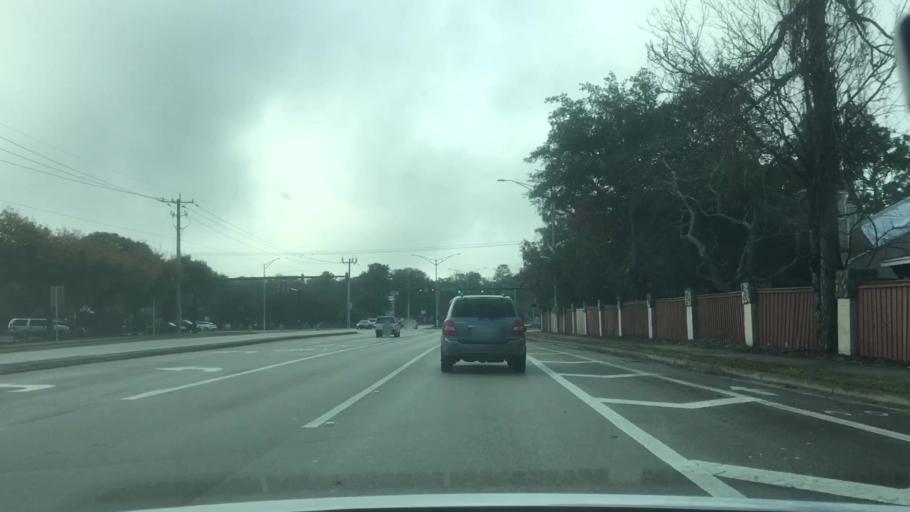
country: US
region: Florida
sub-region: Duval County
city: Atlantic Beach
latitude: 30.3613
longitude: -81.5030
